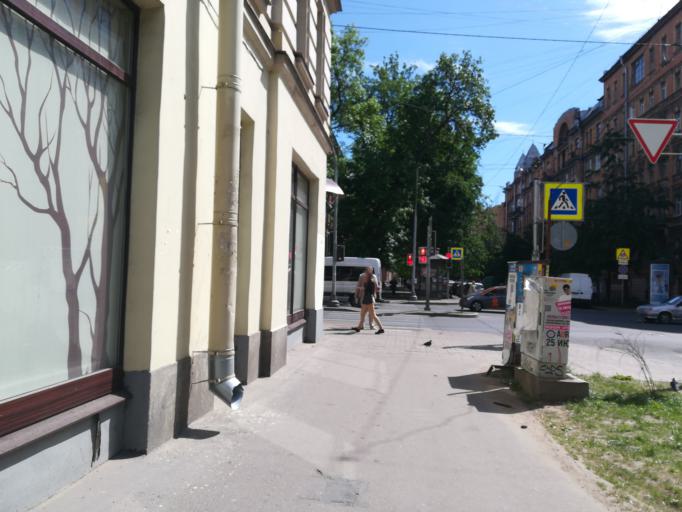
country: RU
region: St.-Petersburg
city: Vasyl'evsky Ostrov
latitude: 59.9457
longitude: 30.2691
